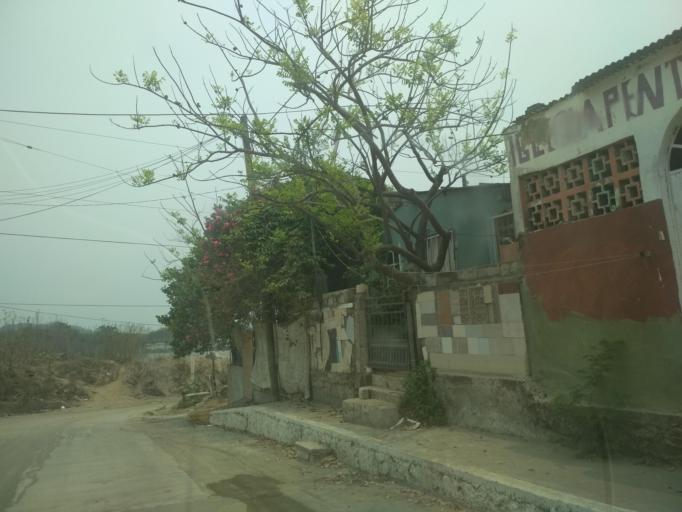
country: MX
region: Veracruz
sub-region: Veracruz
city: Rio Medio [Granja]
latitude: 19.2121
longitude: -96.2086
